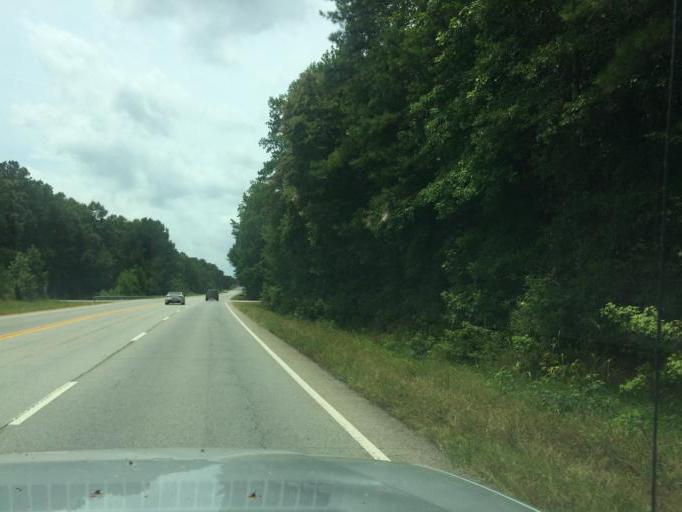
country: US
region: Georgia
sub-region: Hart County
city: Hartwell
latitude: 34.3475
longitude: -82.8213
